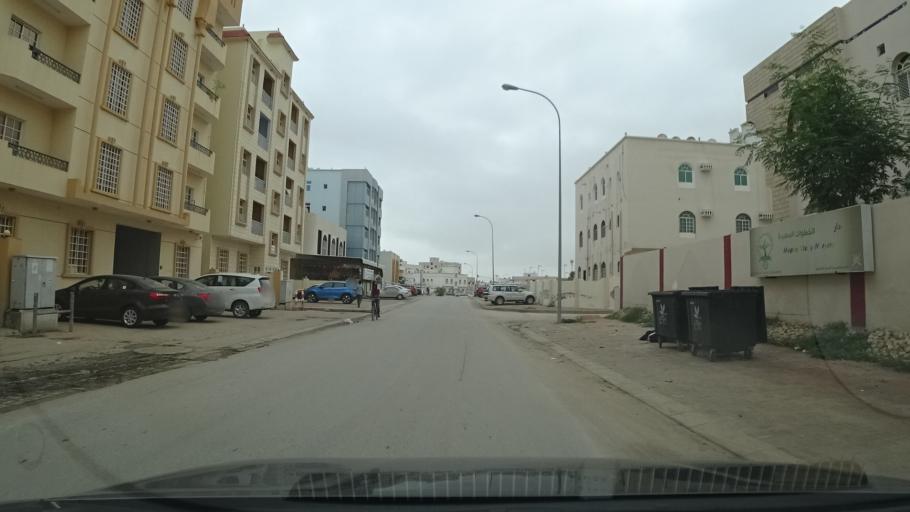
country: OM
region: Zufar
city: Salalah
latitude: 17.0163
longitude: 54.0616
